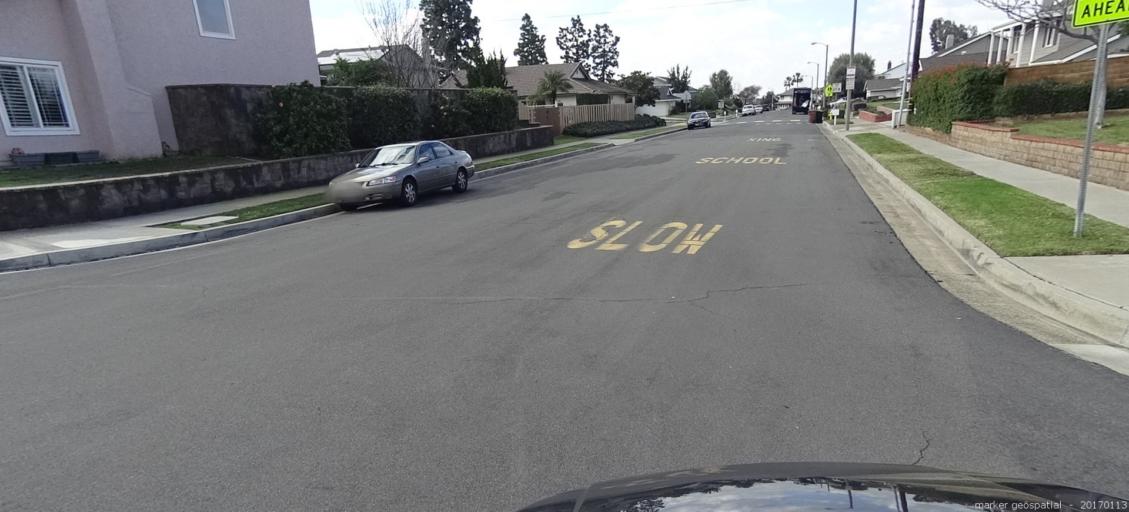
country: US
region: California
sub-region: Orange County
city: Yorba Linda
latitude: 33.8709
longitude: -117.7862
